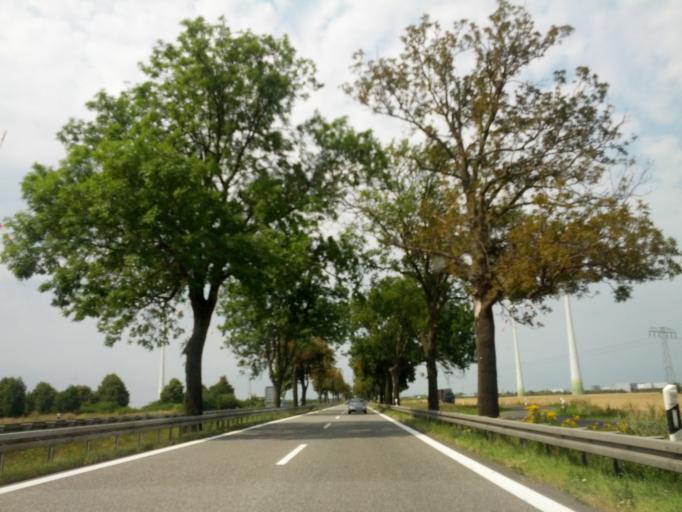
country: DE
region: Brandenburg
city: Nauen
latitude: 52.5830
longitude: 12.9017
